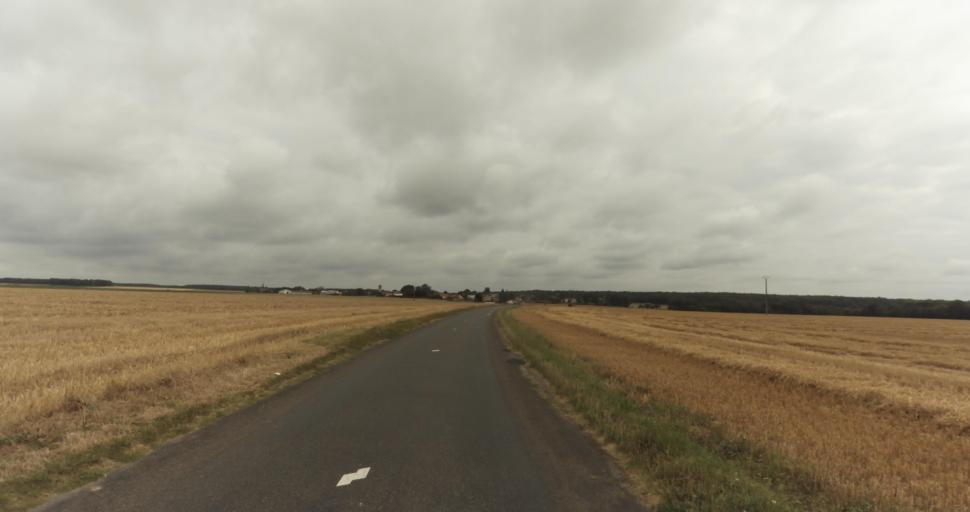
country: FR
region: Haute-Normandie
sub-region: Departement de l'Eure
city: La Couture-Boussey
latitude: 48.9258
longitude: 1.3999
